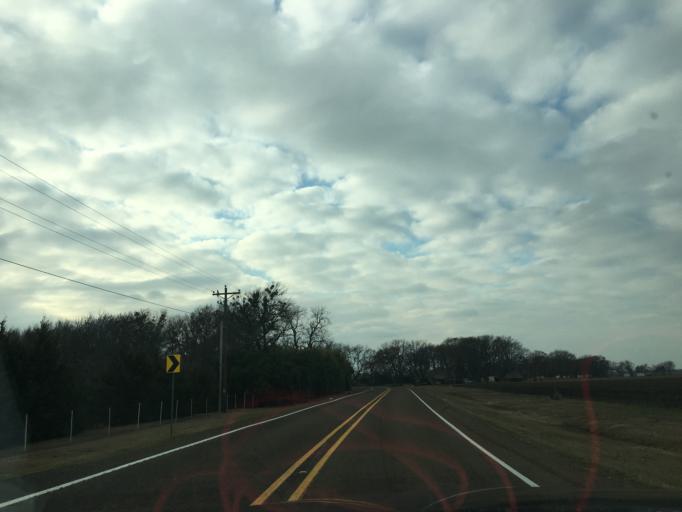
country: US
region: Texas
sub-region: Ellis County
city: Palmer
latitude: 32.4474
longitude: -96.7196
